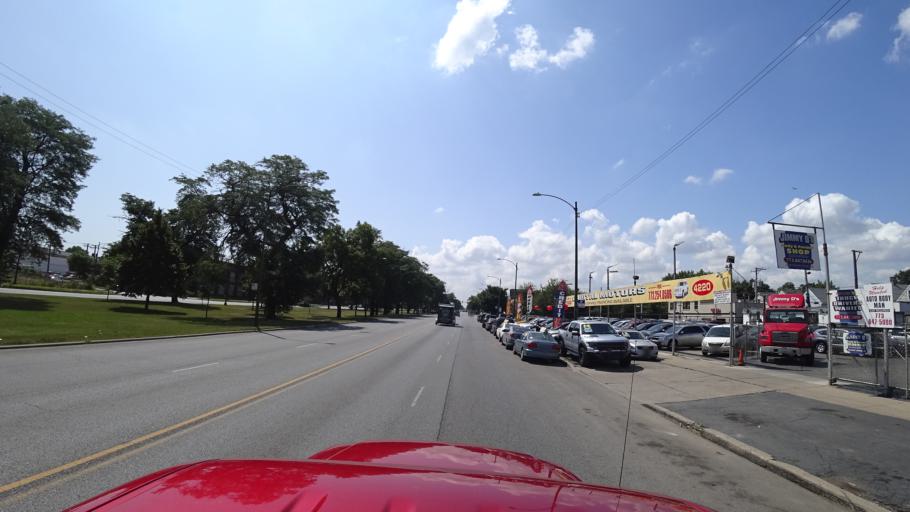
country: US
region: Illinois
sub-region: Cook County
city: Chicago
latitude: 41.8172
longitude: -87.6847
